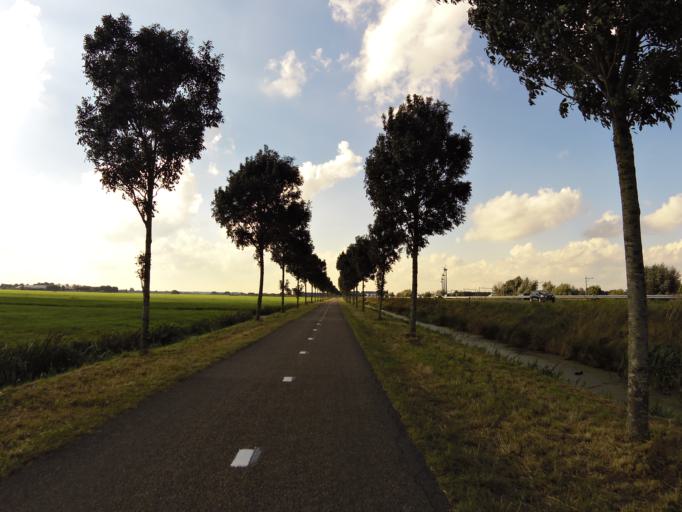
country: NL
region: South Holland
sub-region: Gemeente Leiderdorp
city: Leiderdorp
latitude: 52.1242
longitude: 4.5624
